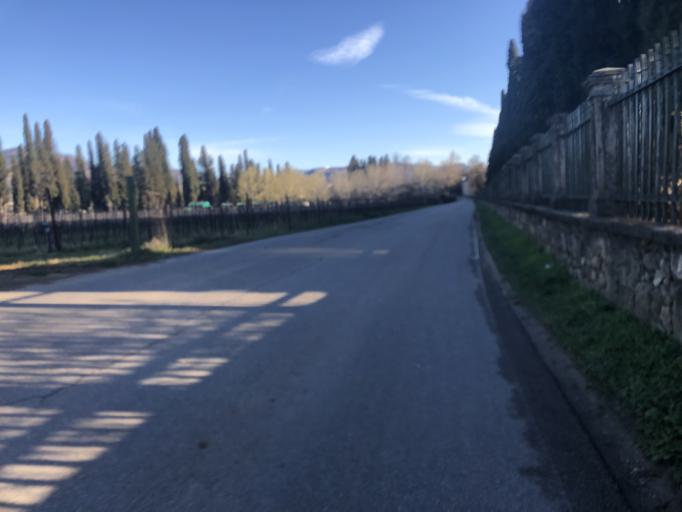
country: IT
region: Veneto
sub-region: Provincia di Verona
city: San Pietro in Cariano
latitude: 45.5066
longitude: 10.8840
